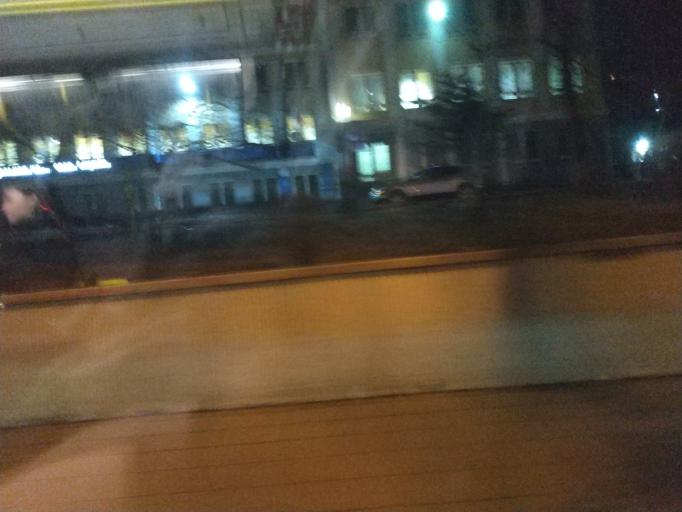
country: RU
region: Primorskiy
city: Vladivostok
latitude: 43.1232
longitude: 131.8883
